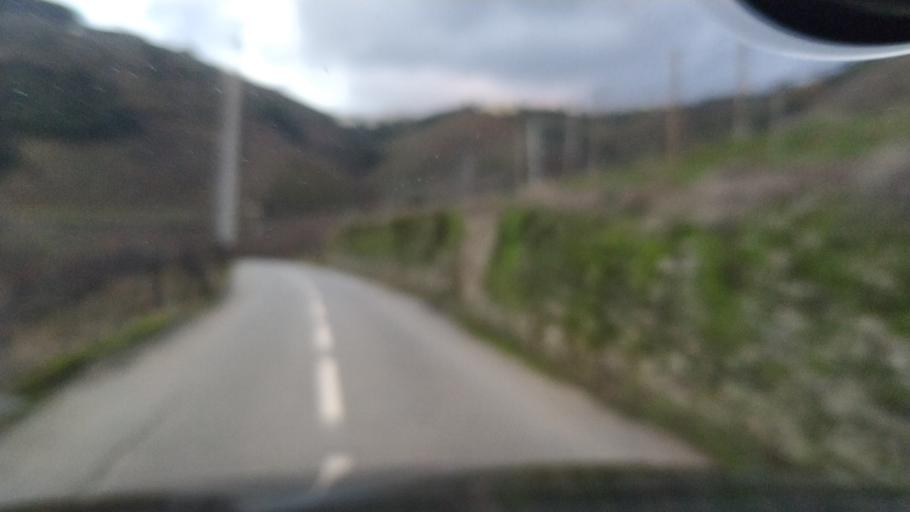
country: PT
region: Vila Real
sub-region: Santa Marta de Penaguiao
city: Santa Marta de Penaguiao
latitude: 41.2399
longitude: -7.7766
